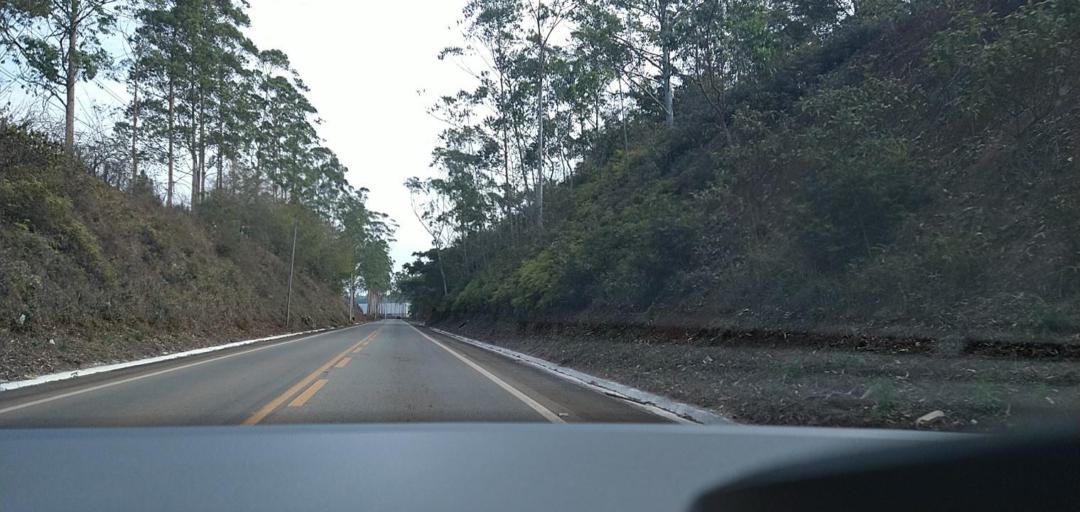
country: BR
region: Minas Gerais
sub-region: Rio Piracicaba
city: Rio Piracicaba
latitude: -19.8820
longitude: -43.1291
